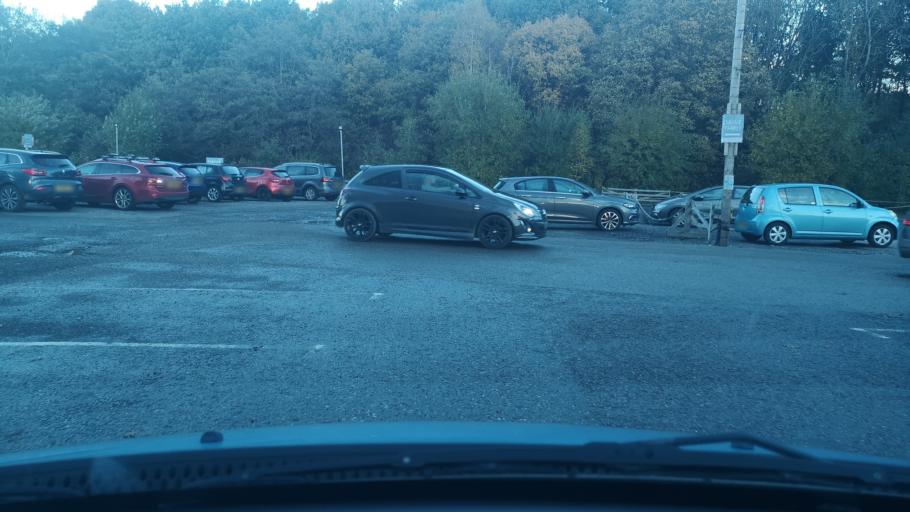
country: GB
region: England
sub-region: City and Borough of Wakefield
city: Crigglestone
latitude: 53.6383
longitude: -1.5472
